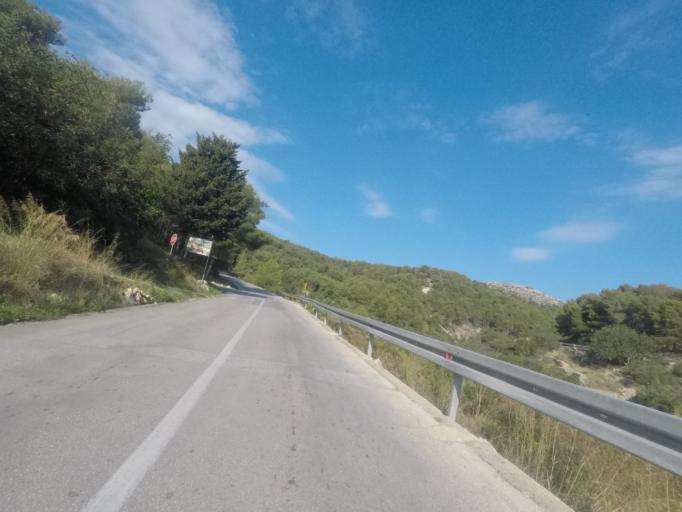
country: HR
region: Splitsko-Dalmatinska
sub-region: Grad Hvar
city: Hvar
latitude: 43.1759
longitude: 16.4436
